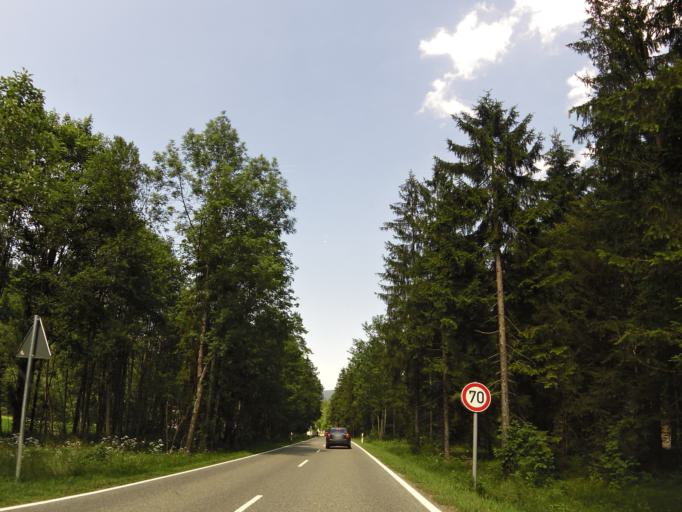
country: DE
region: Bavaria
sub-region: Upper Bavaria
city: Ruhpolding
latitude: 47.7232
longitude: 12.6565
